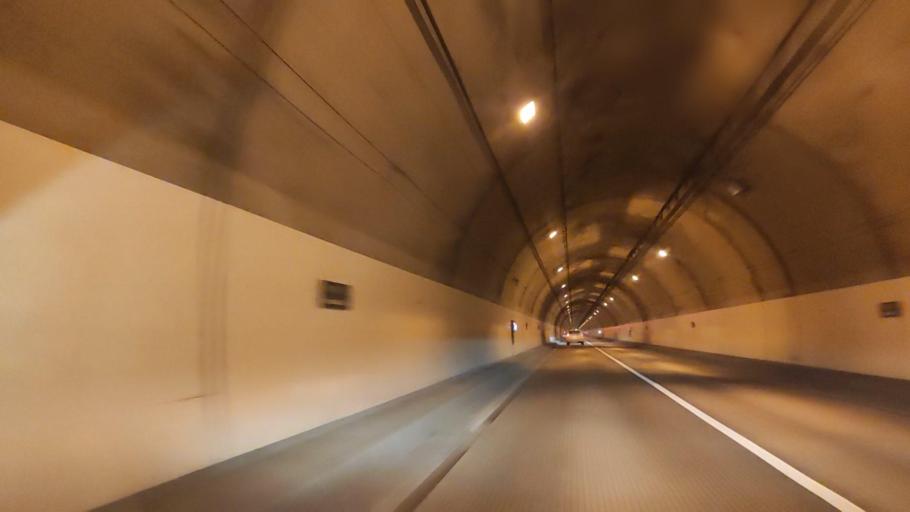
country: JP
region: Hokkaido
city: Ishikari
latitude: 43.4641
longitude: 141.4021
